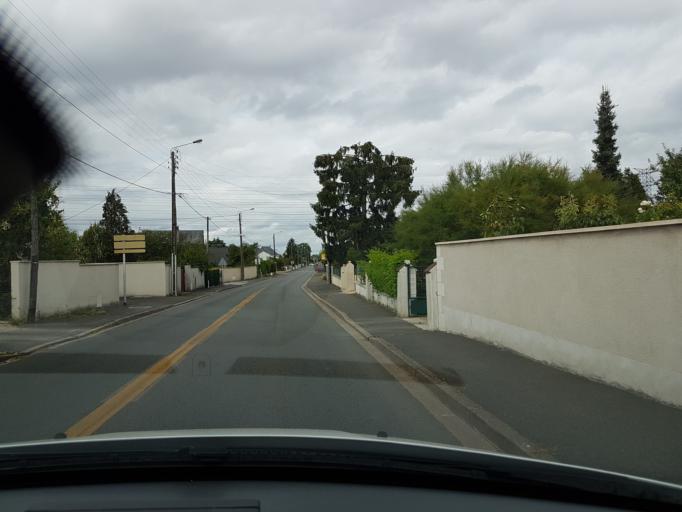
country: FR
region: Centre
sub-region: Departement d'Indre-et-Loire
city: Saint-Avertin
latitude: 47.3476
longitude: 0.7347
